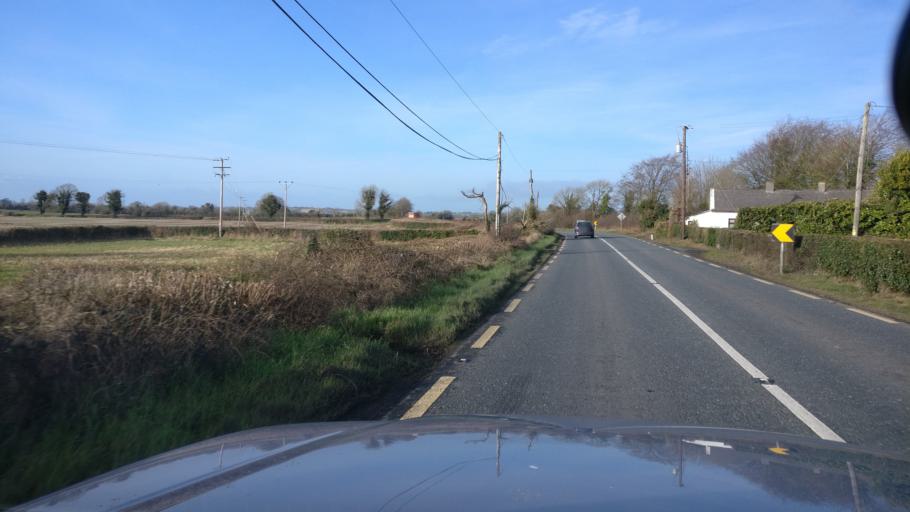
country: IE
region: Leinster
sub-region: Laois
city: Mountmellick
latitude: 53.1595
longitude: -7.3677
